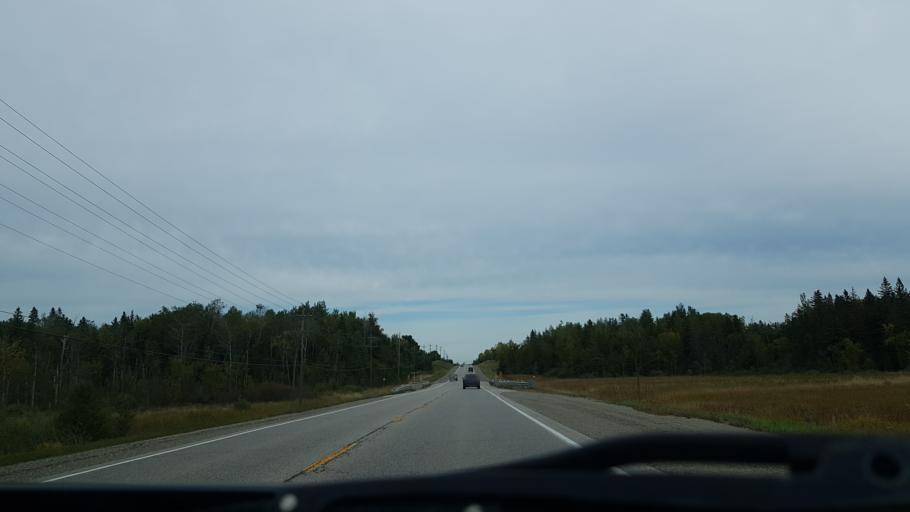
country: CA
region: Ontario
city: Orangeville
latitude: 43.7944
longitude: -80.0684
